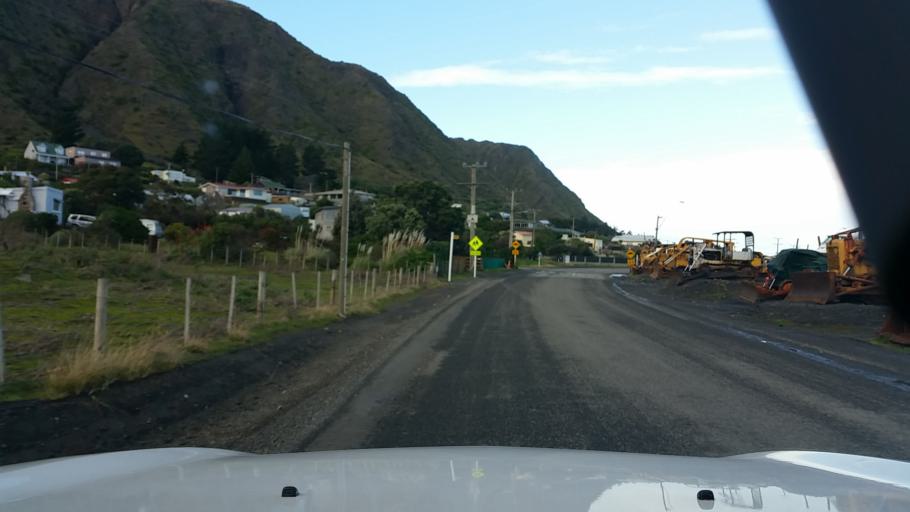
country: NZ
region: Wellington
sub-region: South Wairarapa District
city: Waipawa
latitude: -41.5852
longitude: 175.2346
